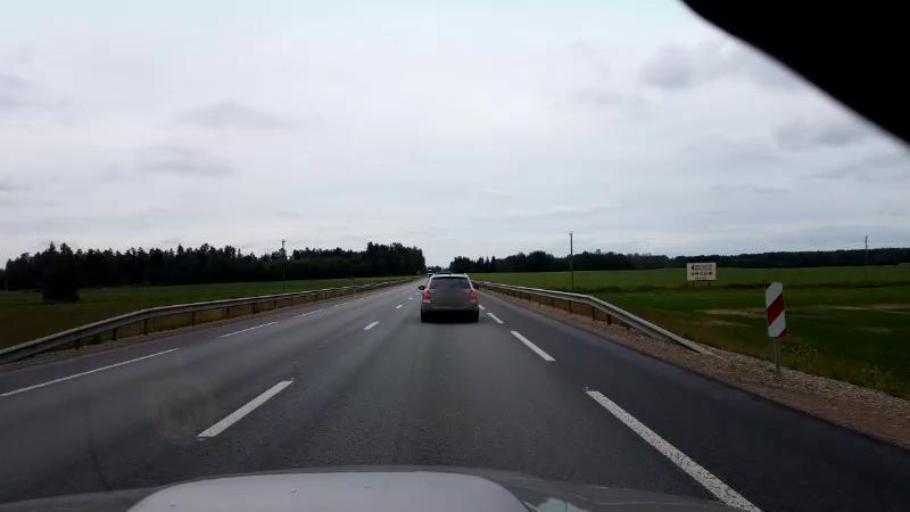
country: LV
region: Lecava
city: Iecava
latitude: 56.6478
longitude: 24.2284
